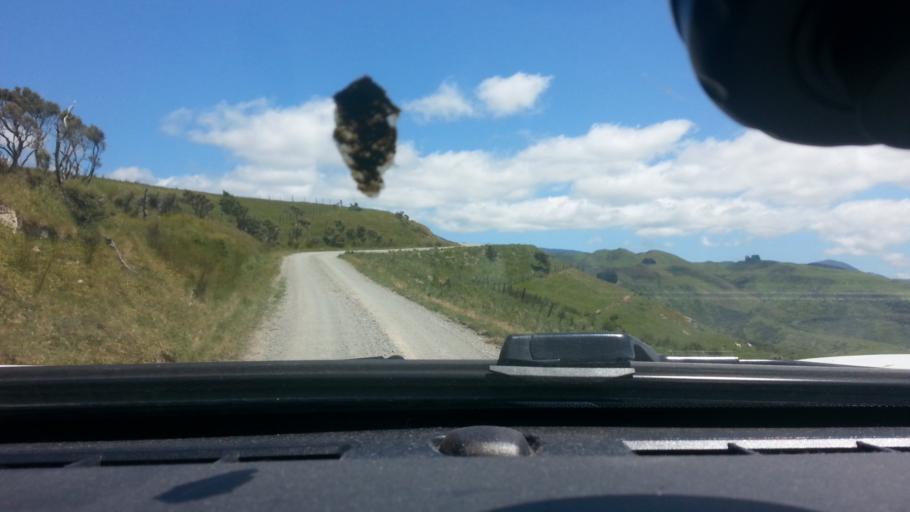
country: NZ
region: Wellington
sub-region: South Wairarapa District
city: Waipawa
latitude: -41.3782
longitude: 175.4707
